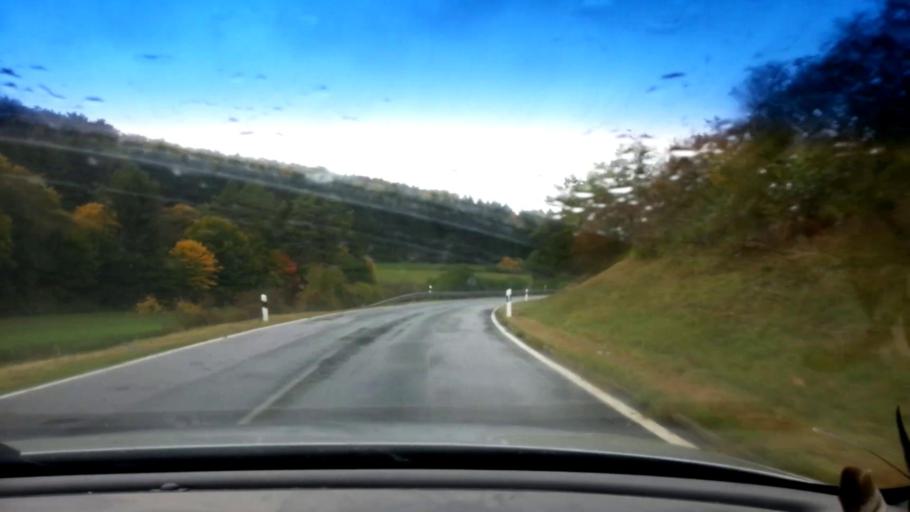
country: DE
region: Bavaria
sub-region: Upper Franconia
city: Heiligenstadt
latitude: 49.8861
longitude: 11.1627
